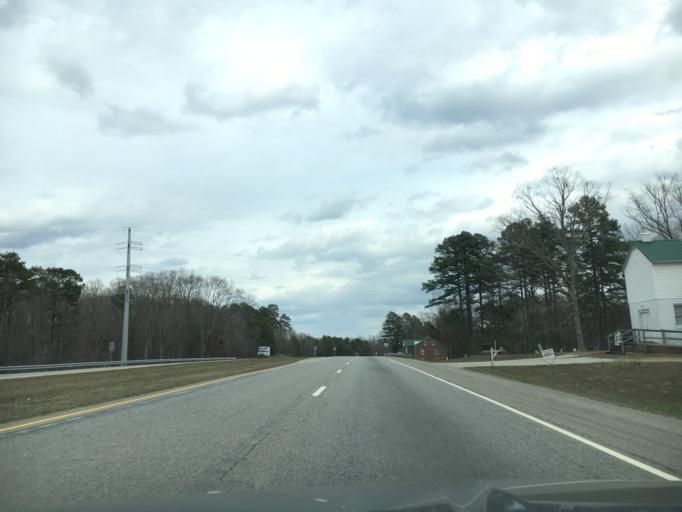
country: US
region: Virginia
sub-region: Mecklenburg County
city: Boydton
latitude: 36.6822
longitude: -78.3485
